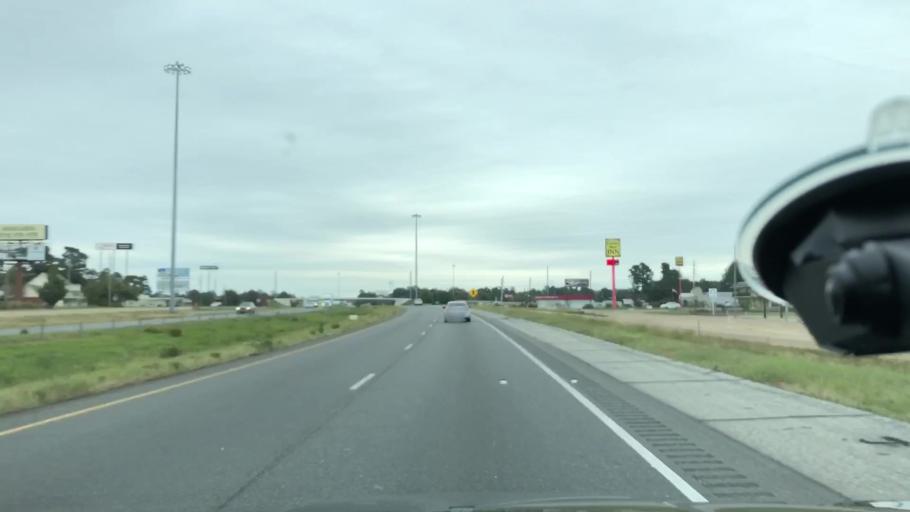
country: US
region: Arkansas
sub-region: Miller County
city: Texarkana
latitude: 33.4701
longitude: -94.0354
